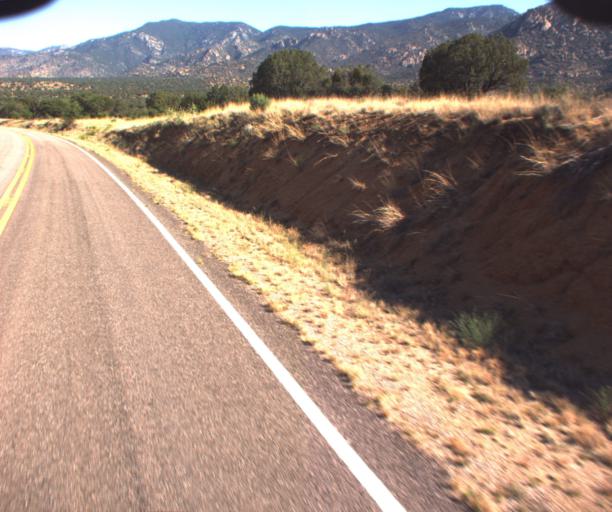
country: US
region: Arizona
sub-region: Graham County
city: Swift Trail Junction
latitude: 32.5926
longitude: -109.8554
